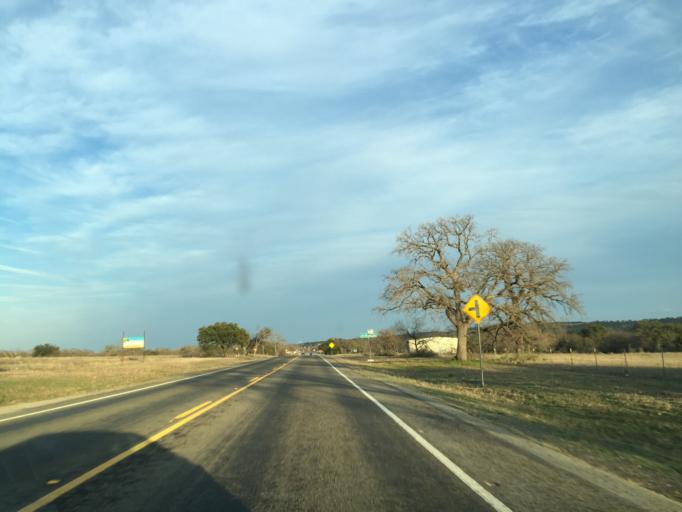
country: US
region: Texas
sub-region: Llano County
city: Buchanan Dam
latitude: 30.7331
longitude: -98.4730
